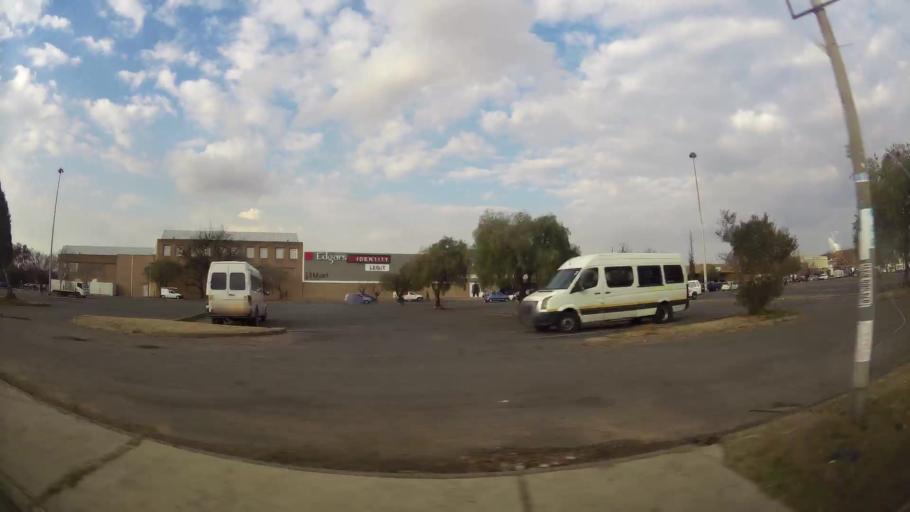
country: ZA
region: Orange Free State
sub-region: Fezile Dabi District Municipality
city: Sasolburg
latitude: -26.8126
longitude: 27.8255
